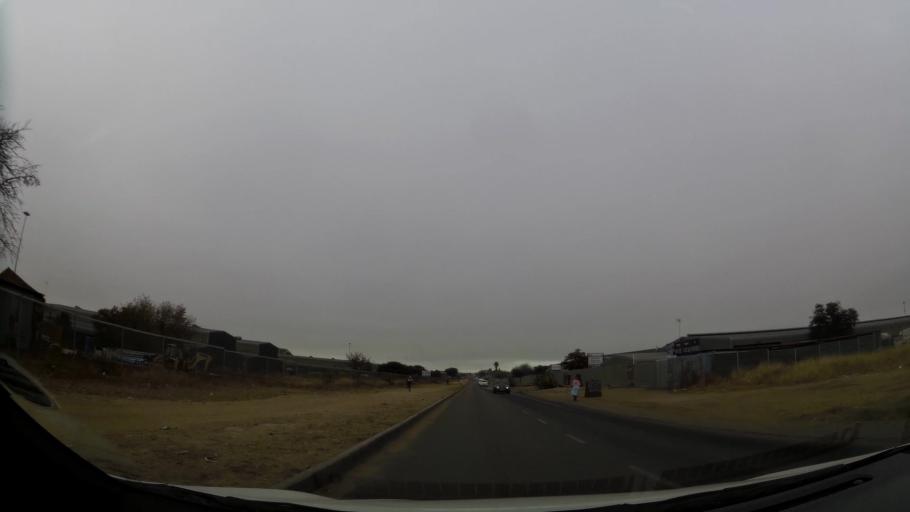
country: ZA
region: Limpopo
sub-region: Capricorn District Municipality
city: Polokwane
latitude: -23.8421
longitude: 29.3997
